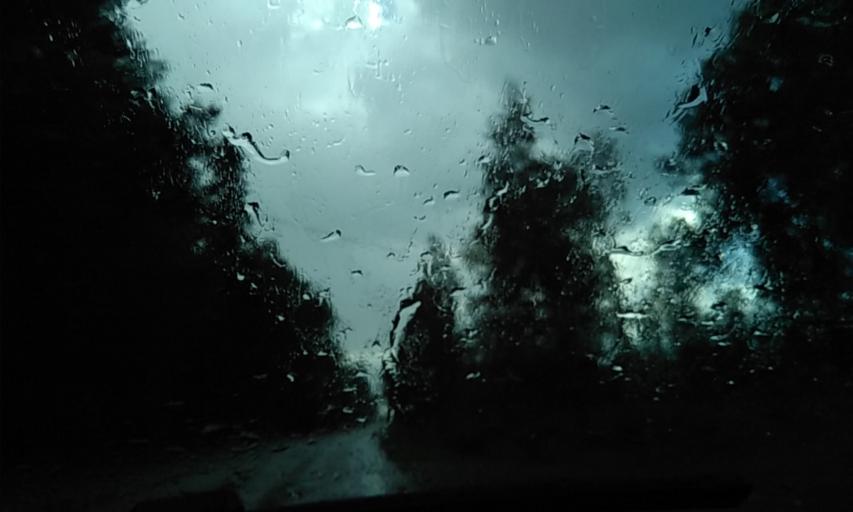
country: SE
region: Vaestra Goetaland
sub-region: Lidkopings Kommun
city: Lidkoping
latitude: 58.5023
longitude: 12.9558
